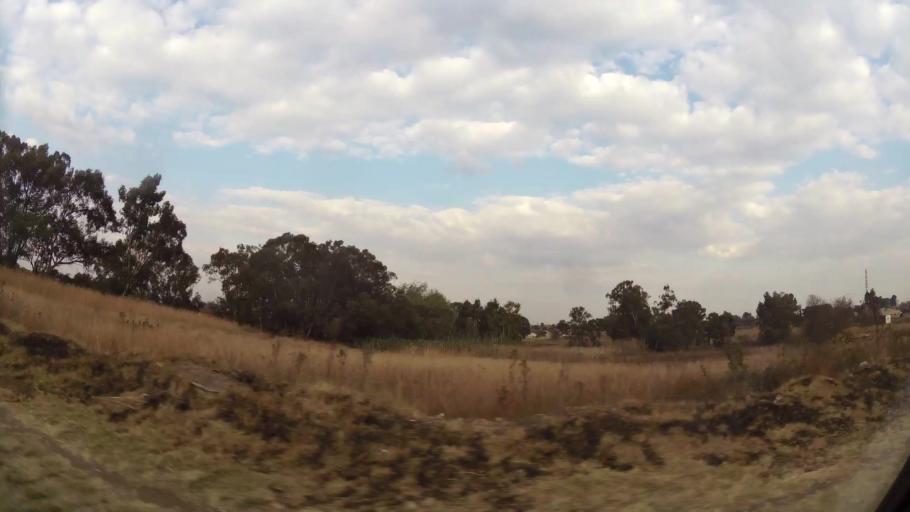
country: ZA
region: Gauteng
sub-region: Ekurhuleni Metropolitan Municipality
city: Germiston
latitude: -26.2484
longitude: 28.1866
